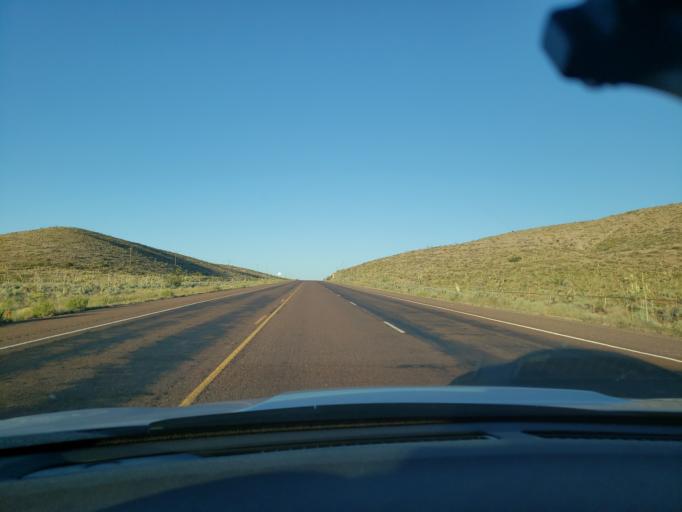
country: US
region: Texas
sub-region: El Paso County
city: Homestead Meadows South
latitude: 31.8270
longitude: -105.8959
